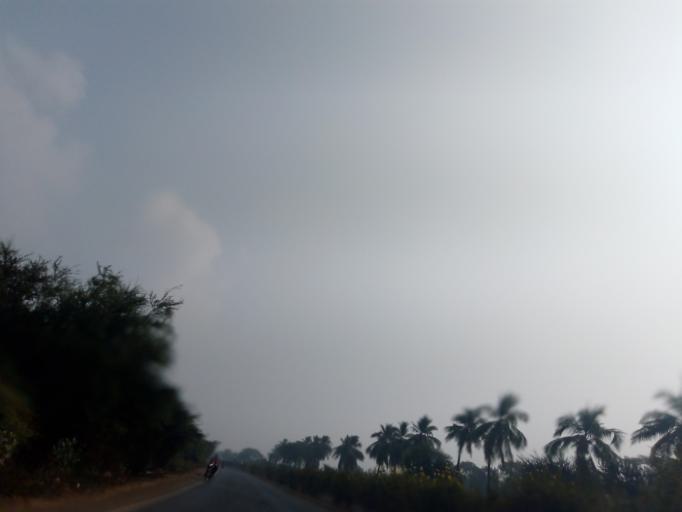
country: IN
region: Andhra Pradesh
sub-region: West Godavari
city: Tadepallegudem
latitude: 16.8120
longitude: 81.3717
